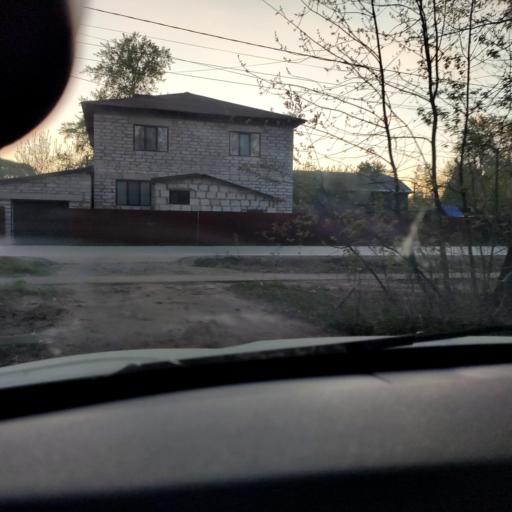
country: RU
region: Perm
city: Krasnokamsk
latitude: 58.0594
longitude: 55.8036
